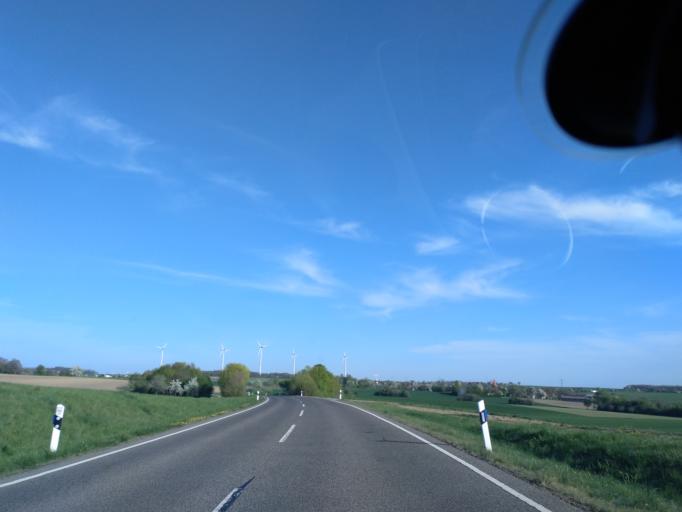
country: DE
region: Baden-Wuerttemberg
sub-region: Regierungsbezirk Stuttgart
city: Langenburg
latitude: 49.2134
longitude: 9.8572
